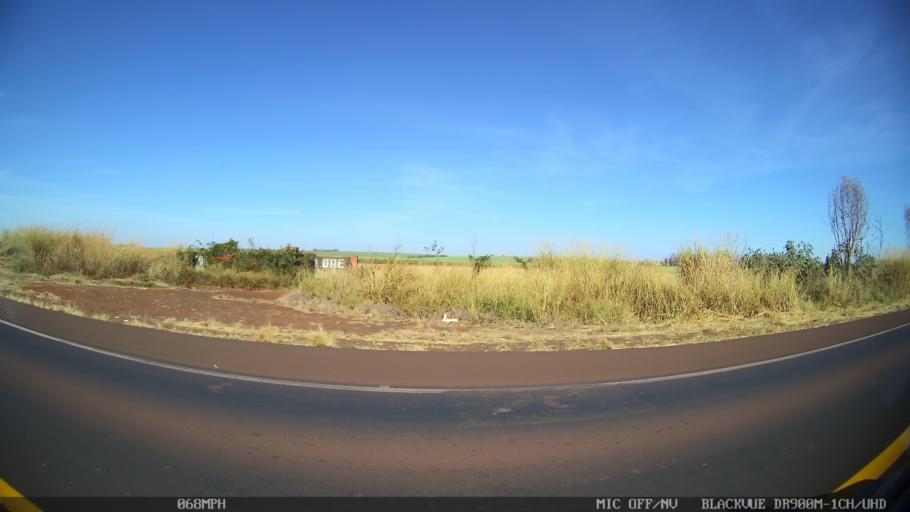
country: BR
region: Sao Paulo
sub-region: Barretos
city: Barretos
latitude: -20.4818
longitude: -48.5057
